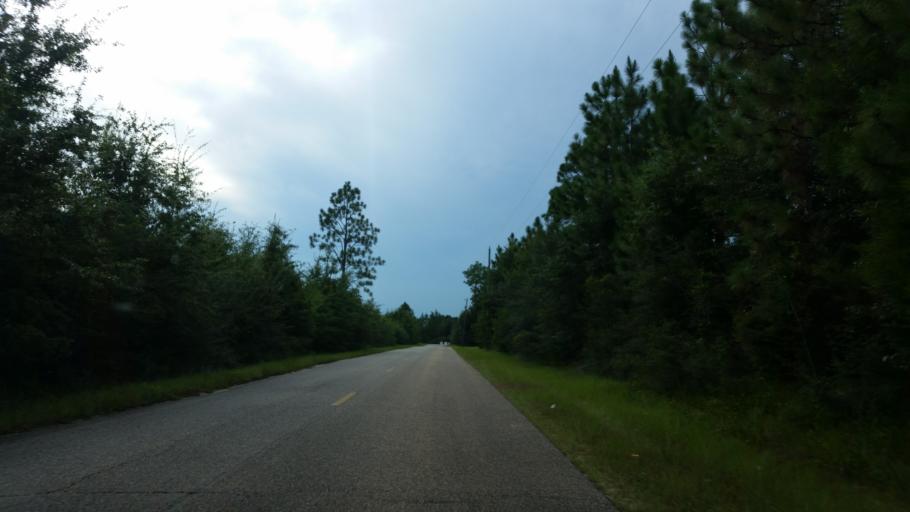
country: US
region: Florida
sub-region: Santa Rosa County
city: Point Baker
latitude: 30.7169
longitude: -86.9607
